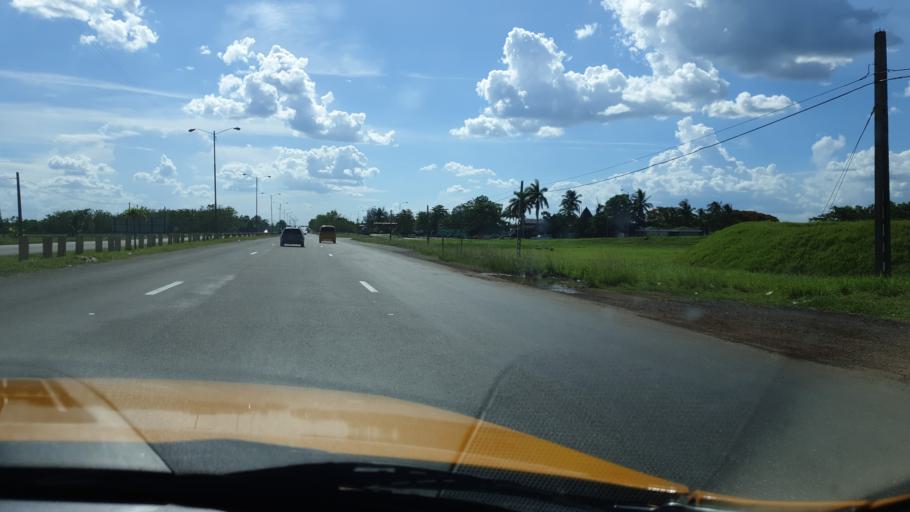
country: CU
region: Cienfuegos
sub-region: Municipio de Aguada de Pasajeros
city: Aguada de Pasajeros
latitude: 22.4038
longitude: -80.8633
